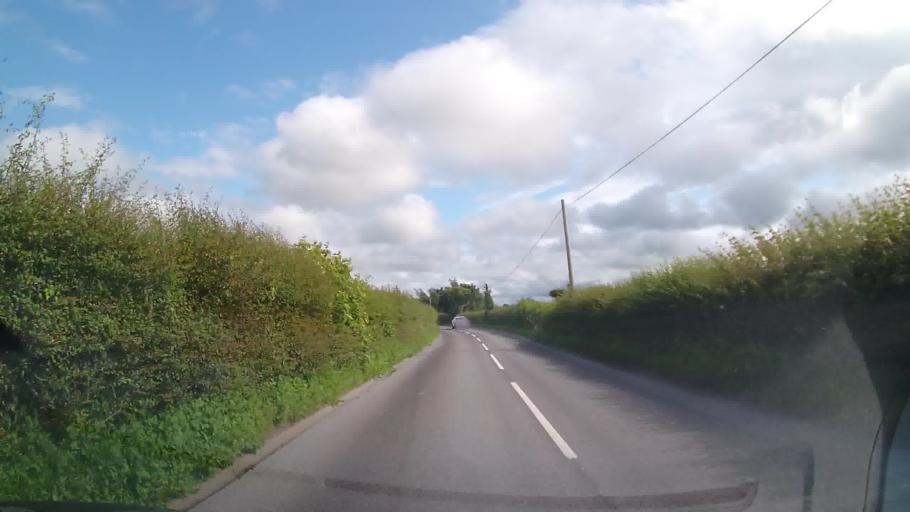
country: GB
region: England
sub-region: Shropshire
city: Pant
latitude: 52.8062
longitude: -3.0267
